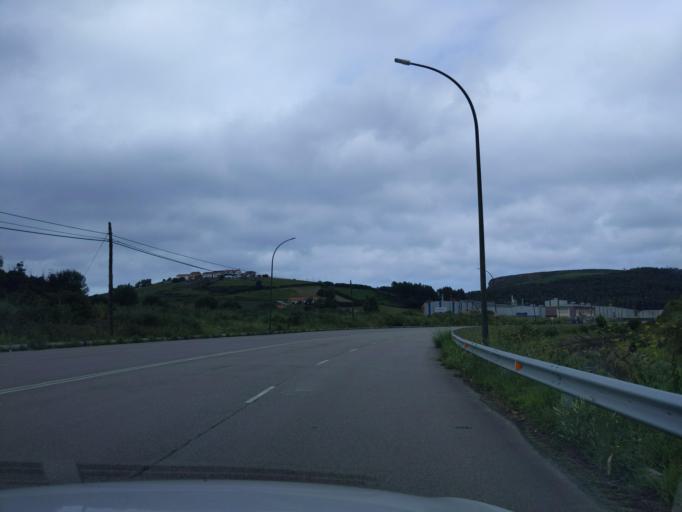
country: ES
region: Asturias
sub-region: Province of Asturias
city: Aviles
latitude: 43.5938
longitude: -5.9157
